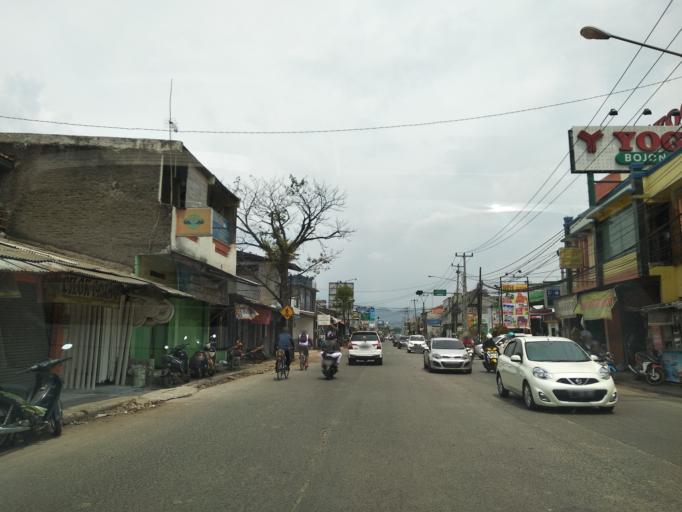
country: ID
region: West Java
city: Pameungpeuk
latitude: -6.9678
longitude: 107.6375
